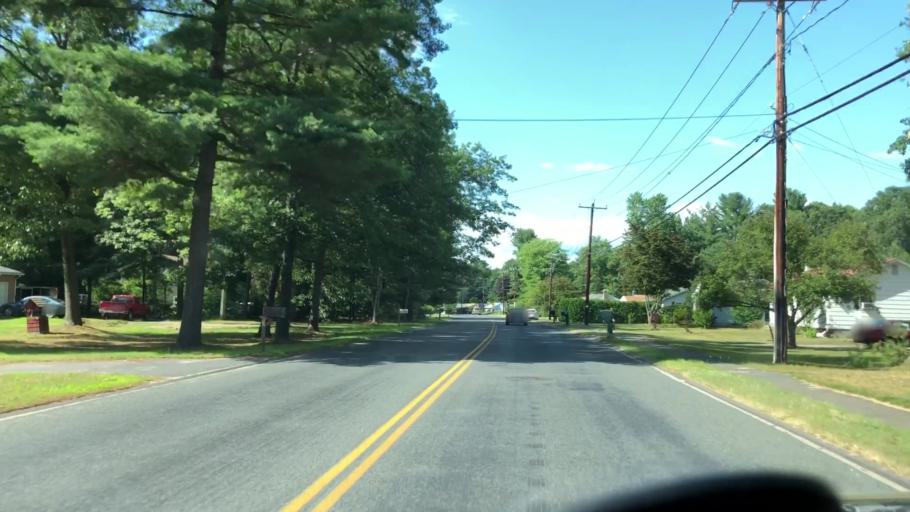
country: US
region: Massachusetts
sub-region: Hampshire County
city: Easthampton
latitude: 42.2315
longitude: -72.6858
